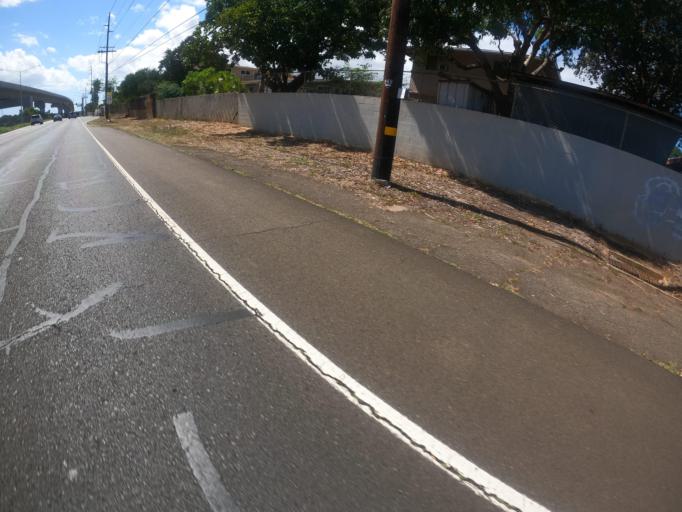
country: US
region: Hawaii
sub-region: Honolulu County
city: Waipahu
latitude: 21.3902
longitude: -157.9940
